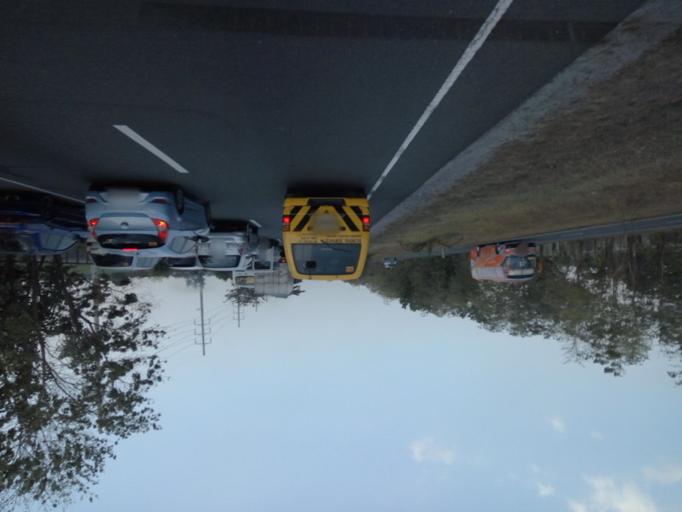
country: PH
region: Central Luzon
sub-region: Province of Pampanga
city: Bulaon
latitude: 15.1020
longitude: 120.6653
